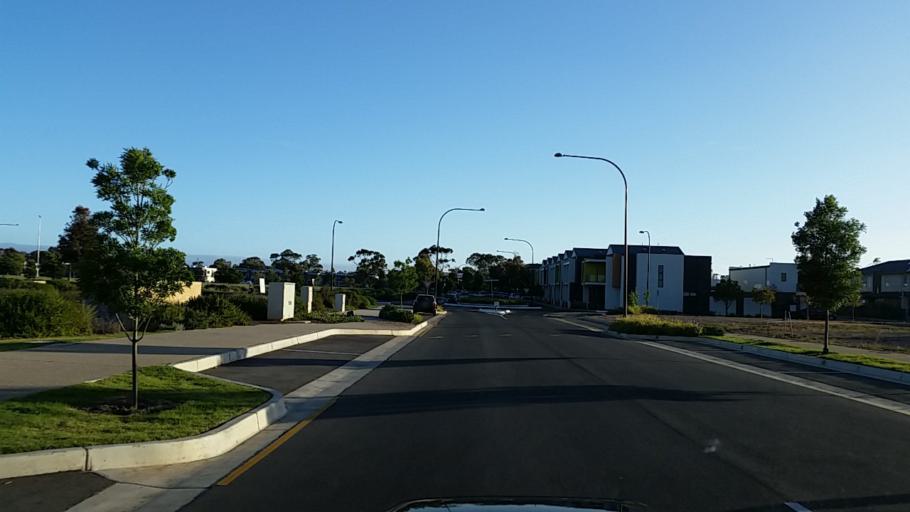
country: AU
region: South Australia
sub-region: Charles Sturt
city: Woodville North
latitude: -34.8707
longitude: 138.5344
